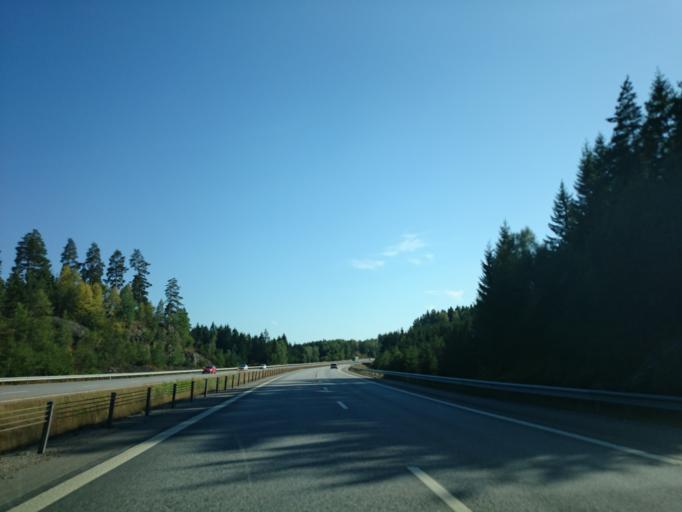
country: SE
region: Soedermanland
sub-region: Trosa Kommun
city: Vagnharad
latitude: 58.9783
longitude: 17.5292
